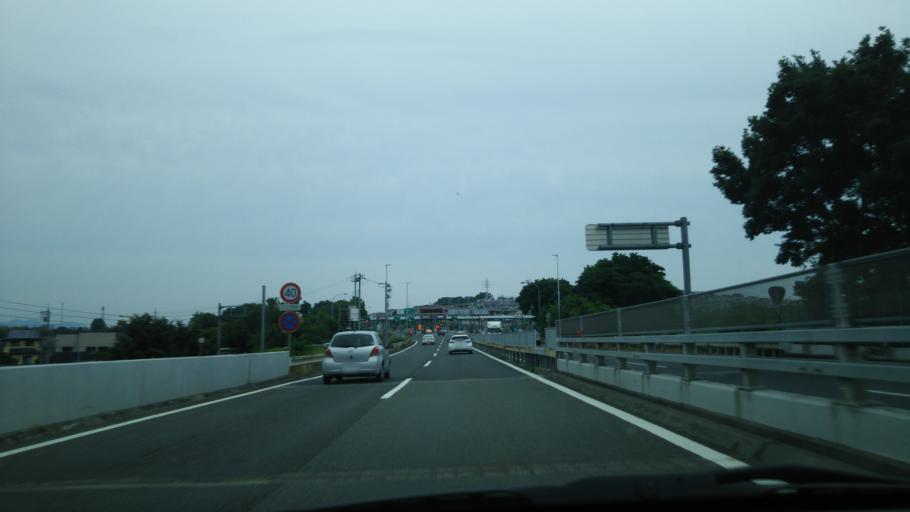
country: JP
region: Kanagawa
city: Oiso
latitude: 35.3344
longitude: 139.2940
